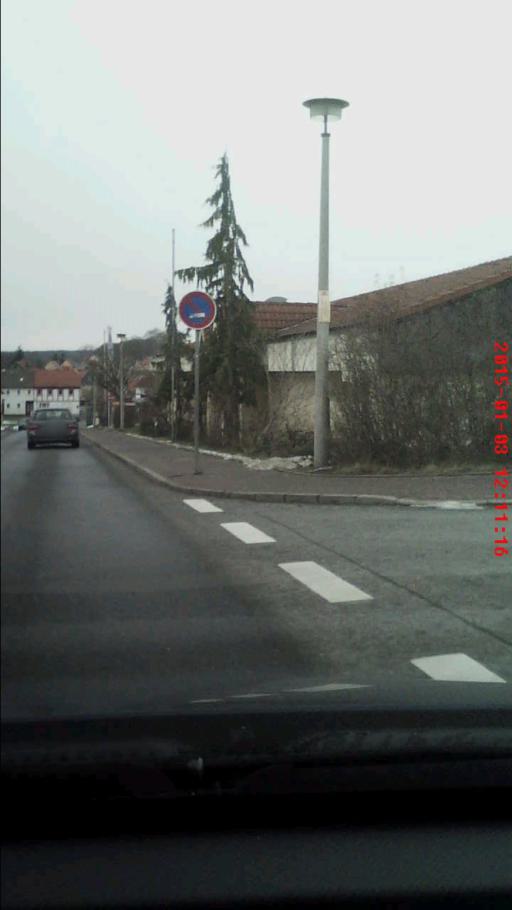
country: DE
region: Thuringia
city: Blankenhain
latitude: 50.8571
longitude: 11.3479
